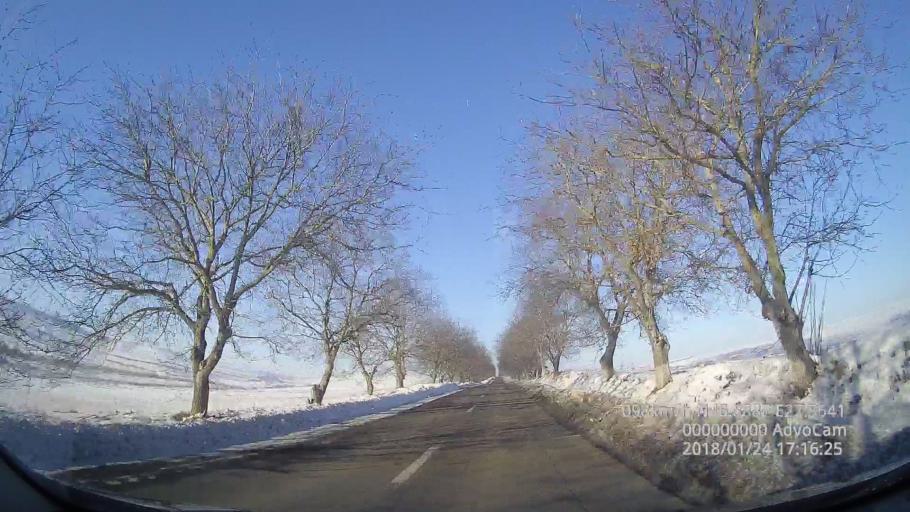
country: RO
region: Vaslui
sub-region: Comuna Rebricea
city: Rebricea
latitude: 46.8894
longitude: 27.5641
